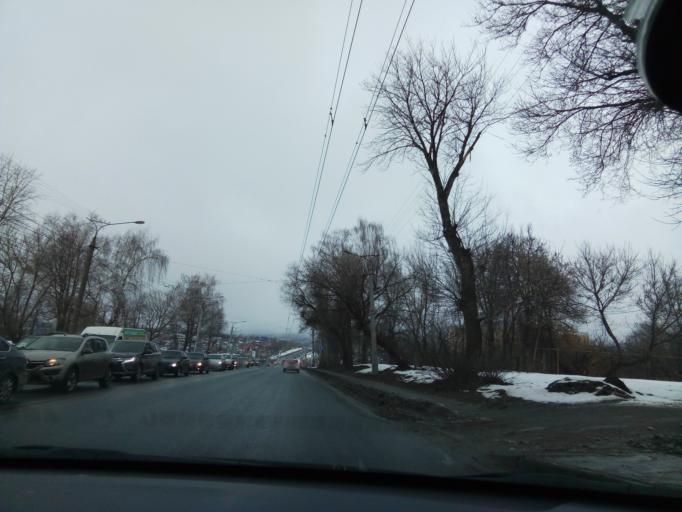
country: RU
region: Chuvashia
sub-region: Cheboksarskiy Rayon
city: Cheboksary
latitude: 56.1240
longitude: 47.2268
